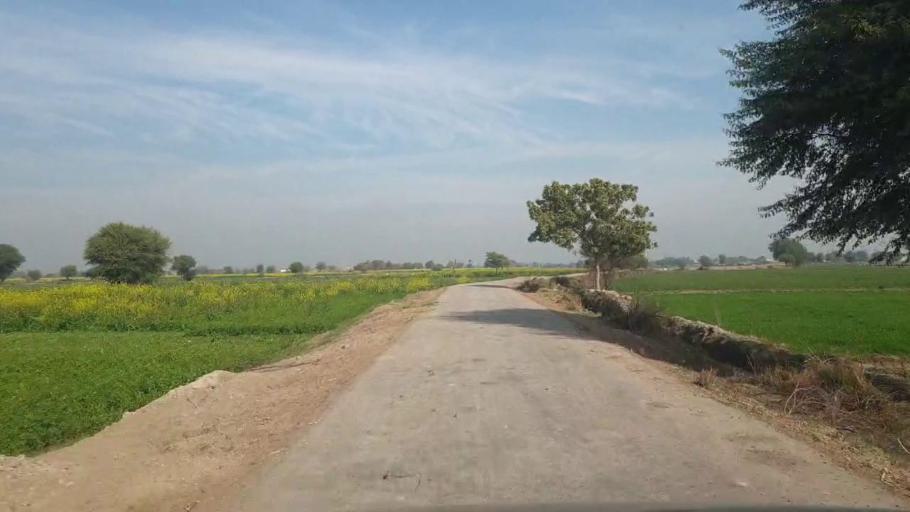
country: PK
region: Sindh
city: Shahpur Chakar
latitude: 26.1802
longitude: 68.5797
